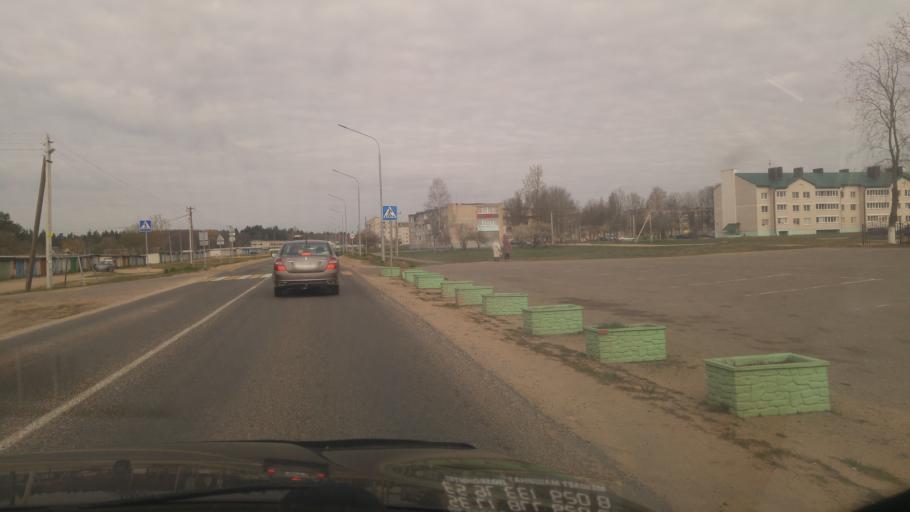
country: BY
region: Minsk
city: Chervyen'
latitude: 53.7002
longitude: 28.4162
